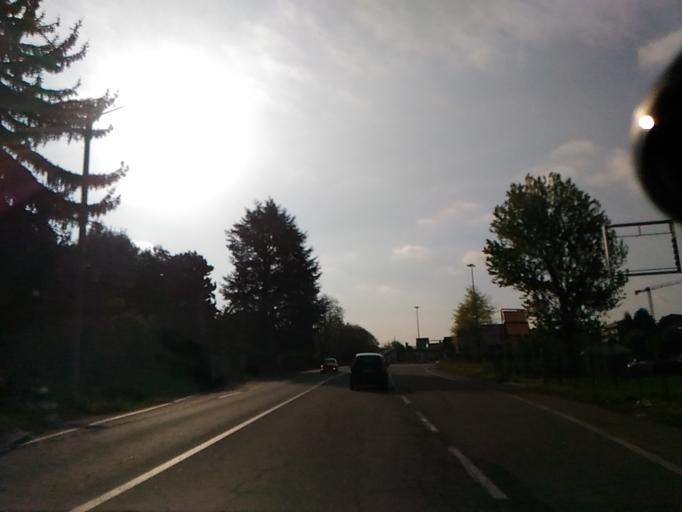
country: IT
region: Lombardy
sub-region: Provincia di Varese
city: Busto Arsizio
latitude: 45.6265
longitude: 8.8471
